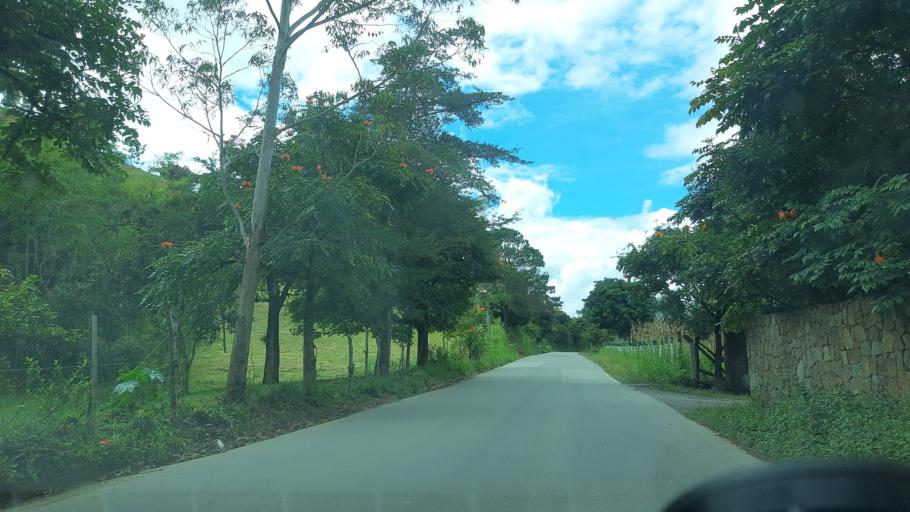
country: CO
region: Boyaca
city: Garagoa
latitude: 5.0568
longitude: -73.3840
